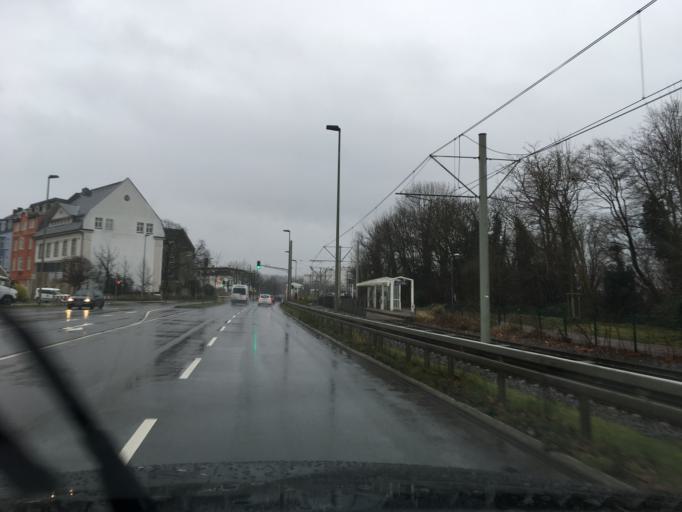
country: DE
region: North Rhine-Westphalia
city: Hattingen
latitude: 51.4012
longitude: 7.1730
